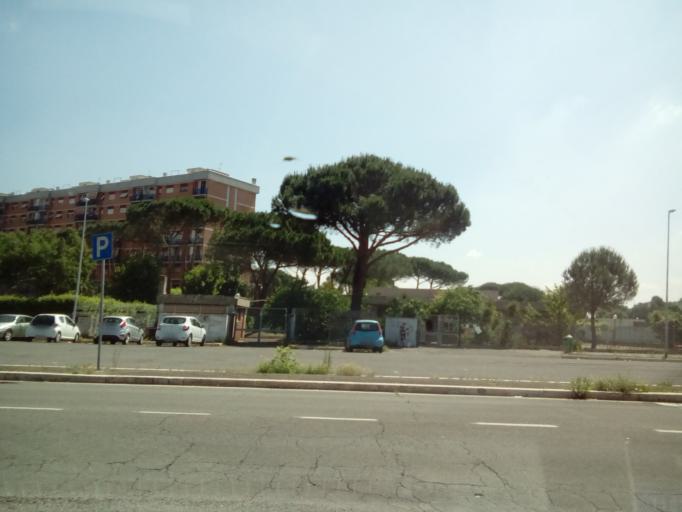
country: IT
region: Latium
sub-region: Citta metropolitana di Roma Capitale
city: Rome
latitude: 41.8807
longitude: 12.5848
